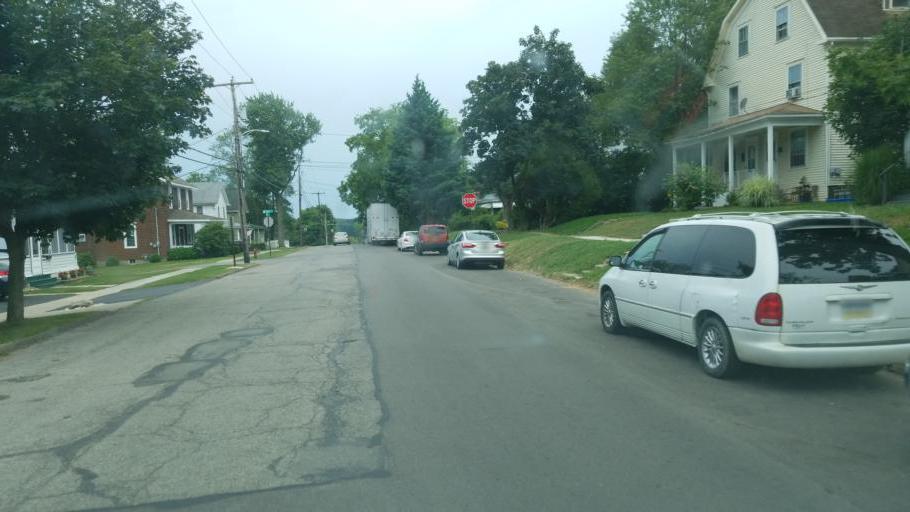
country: US
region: Pennsylvania
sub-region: Clarion County
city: Clarion
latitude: 41.2125
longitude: -79.3893
